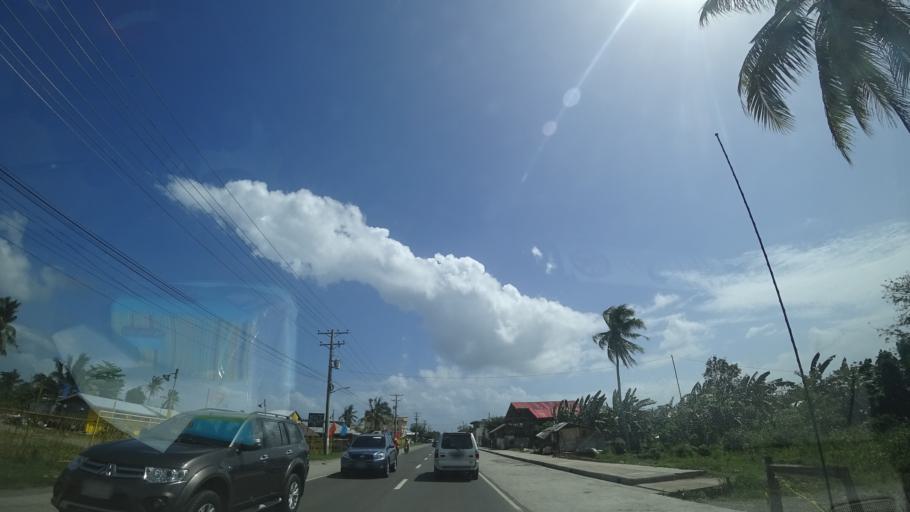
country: PH
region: Eastern Visayas
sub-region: Province of Leyte
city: Pawing
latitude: 11.1816
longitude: 124.9999
